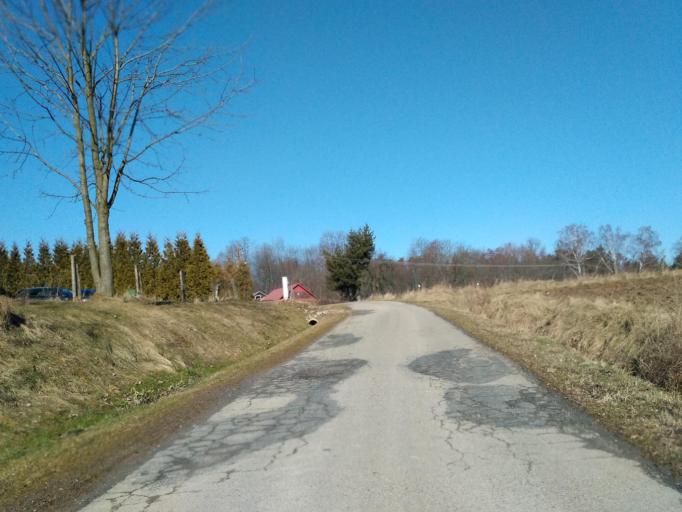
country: PL
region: Subcarpathian Voivodeship
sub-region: Powiat rzeszowski
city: Siedliska
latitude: 49.9376
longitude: 21.9472
